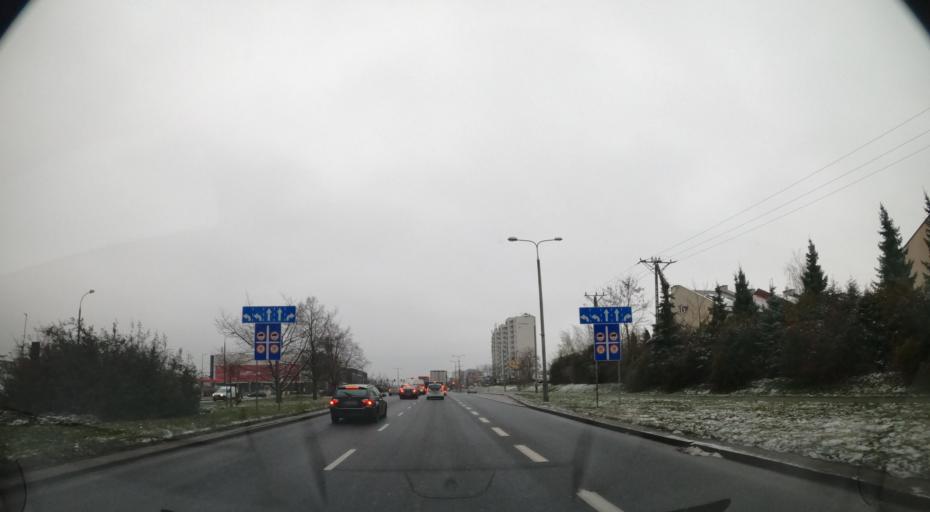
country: PL
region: Masovian Voivodeship
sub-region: Plock
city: Plock
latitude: 52.5347
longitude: 19.7624
